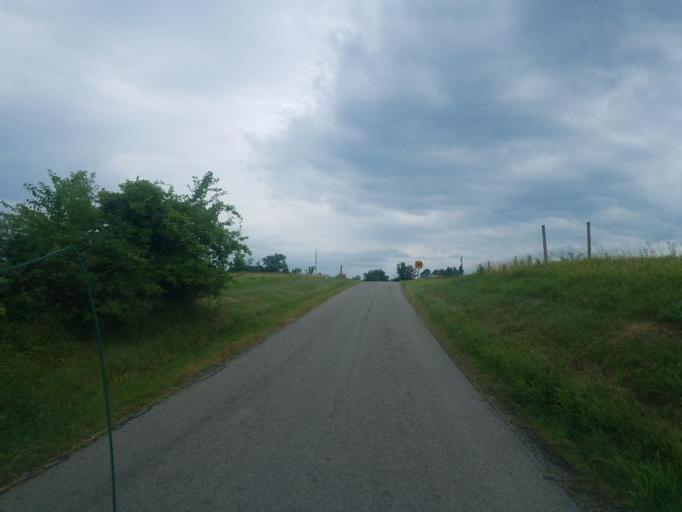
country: US
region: Ohio
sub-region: Defiance County
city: Hicksville
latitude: 41.3022
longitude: -84.8039
